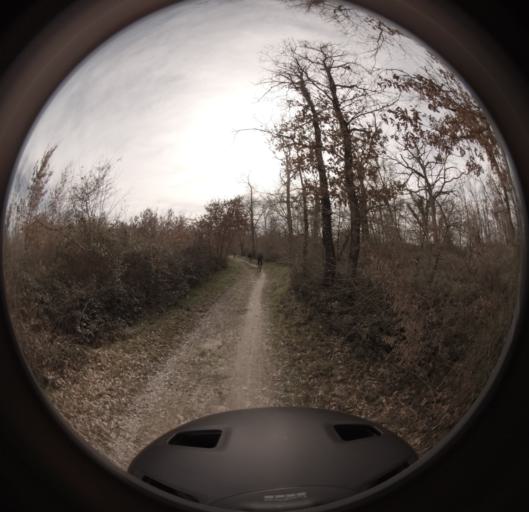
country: FR
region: Midi-Pyrenees
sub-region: Departement du Tarn-et-Garonne
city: Montech
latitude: 43.9576
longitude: 1.2591
